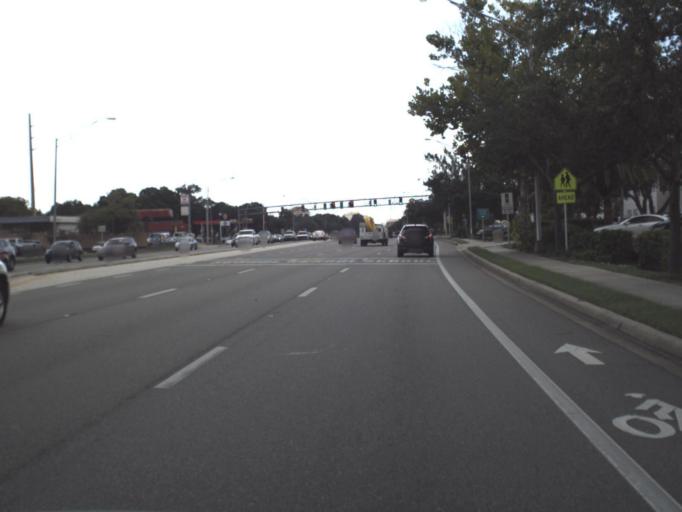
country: US
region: Florida
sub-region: Sarasota County
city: Sarasota
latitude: 27.3377
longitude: -82.5122
